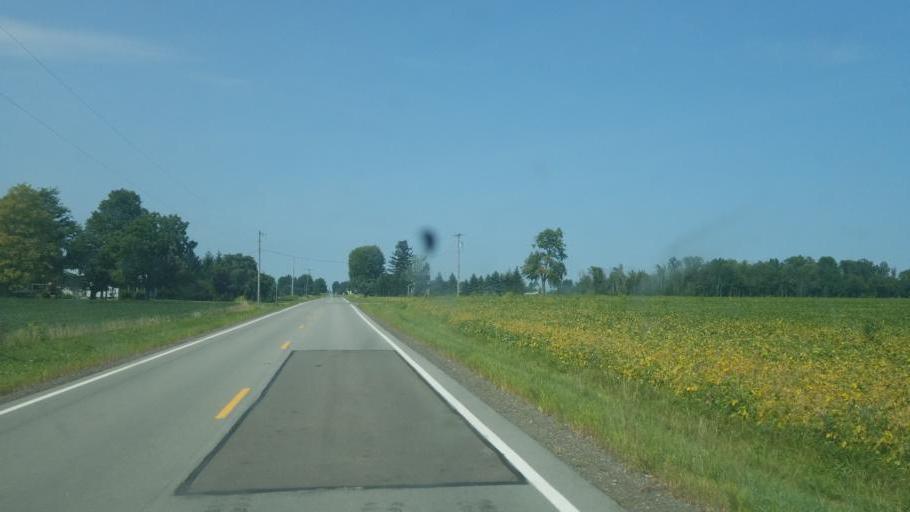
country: US
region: Ohio
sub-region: Crawford County
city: Crestline
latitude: 40.8245
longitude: -82.7301
